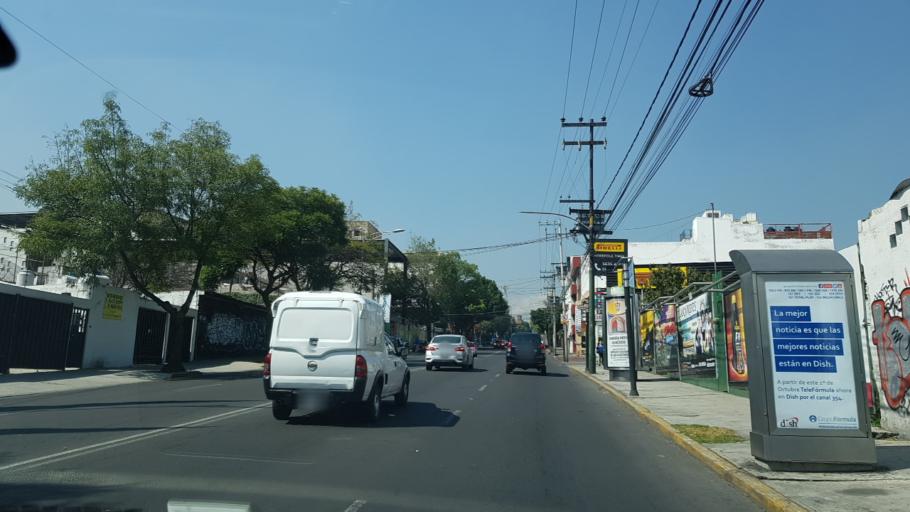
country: MX
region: Mexico City
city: Magdalena Contreras
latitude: 19.3492
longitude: -99.2256
